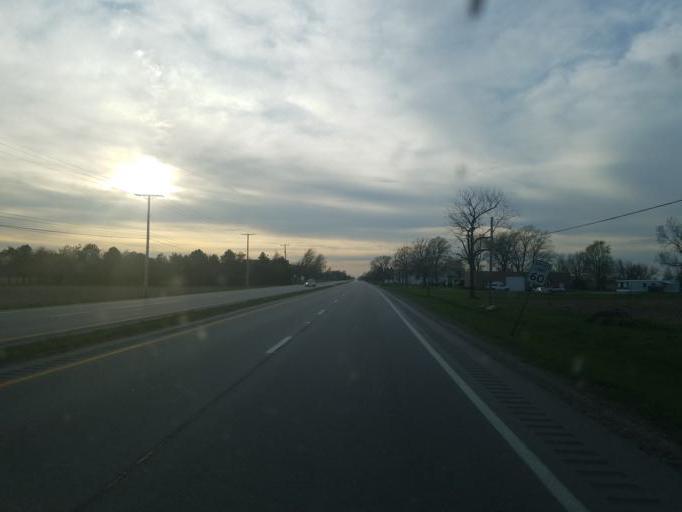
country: US
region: Ohio
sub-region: Sandusky County
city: Gibsonburg
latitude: 41.4038
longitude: -83.2481
